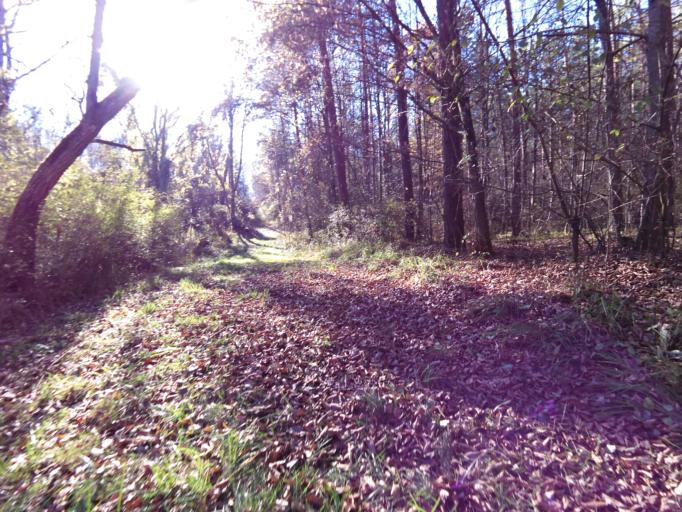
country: DE
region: Bavaria
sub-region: Upper Bavaria
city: Wang
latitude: 48.5028
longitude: 11.9804
